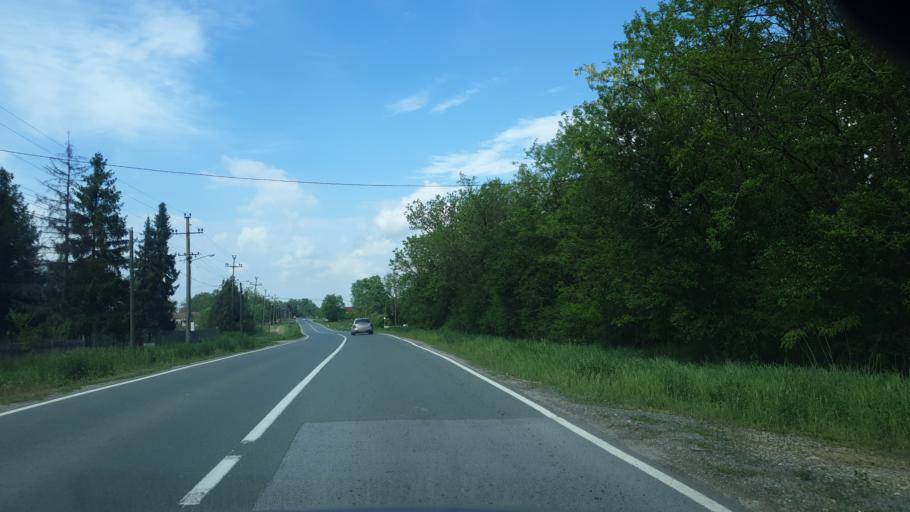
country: RS
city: Stubline
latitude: 44.5979
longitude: 20.1467
